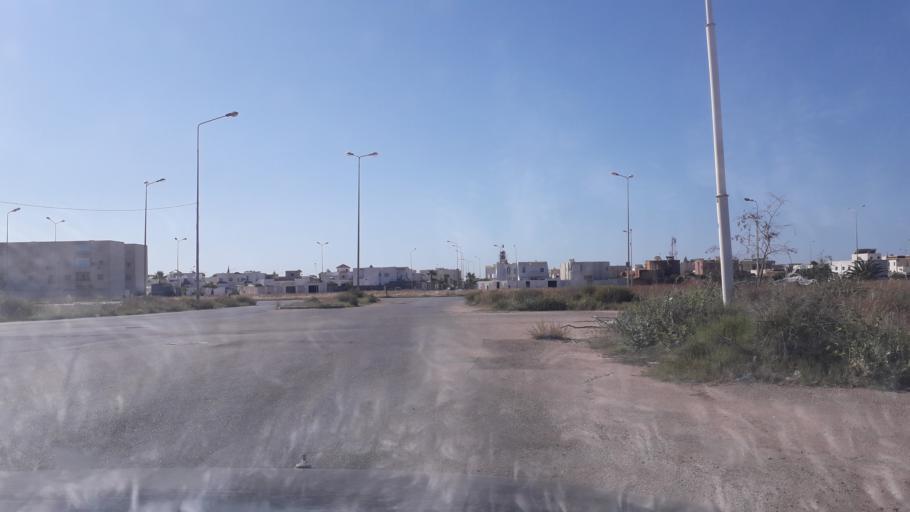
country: TN
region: Safaqis
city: Al Qarmadah
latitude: 34.8325
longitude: 10.7551
